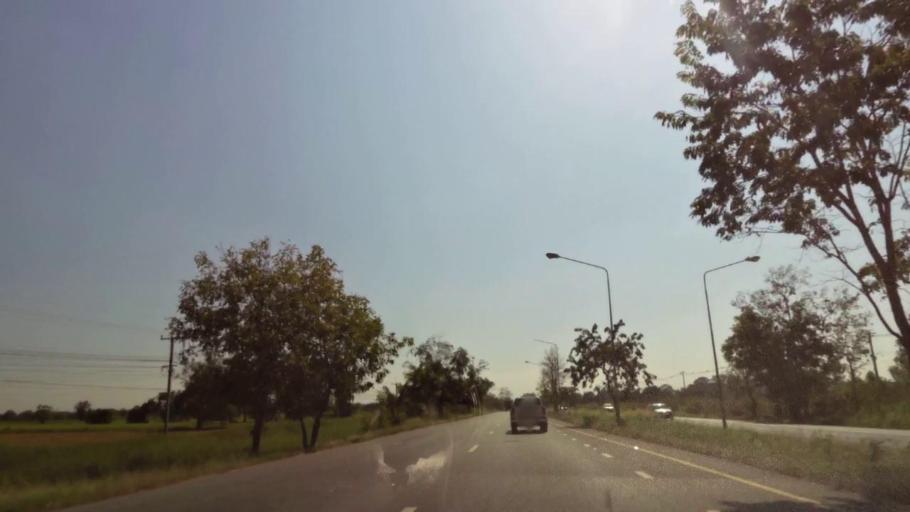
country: TH
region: Nakhon Sawan
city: Kao Liao
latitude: 15.8620
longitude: 100.1168
